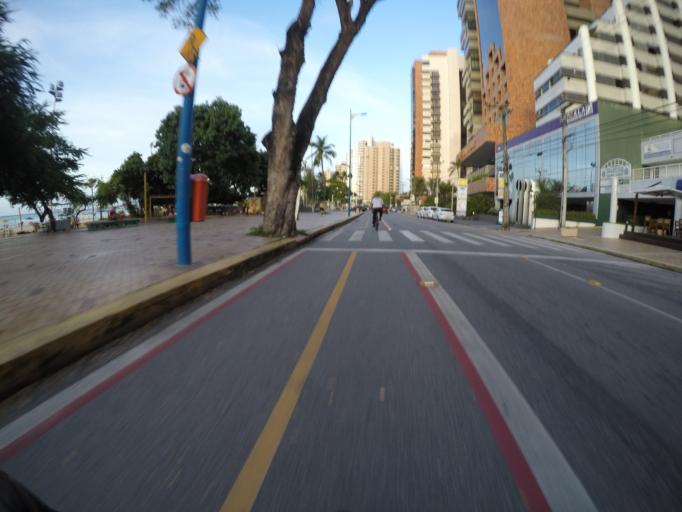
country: BR
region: Ceara
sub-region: Fortaleza
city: Fortaleza
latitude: -3.7232
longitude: -38.4859
